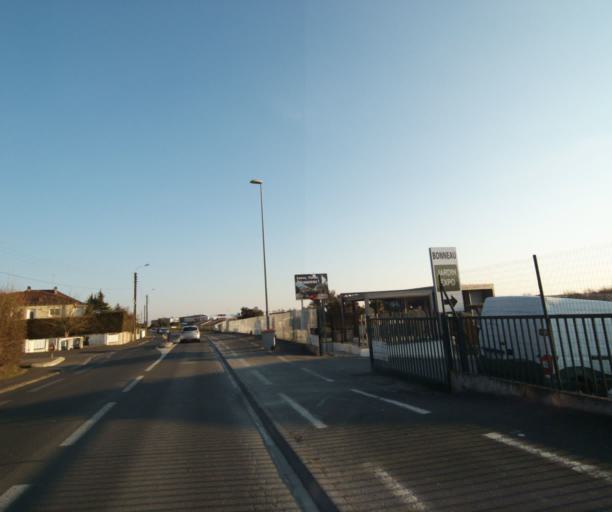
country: FR
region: Poitou-Charentes
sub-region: Departement des Deux-Sevres
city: Niort
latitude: 46.3069
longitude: -0.4416
